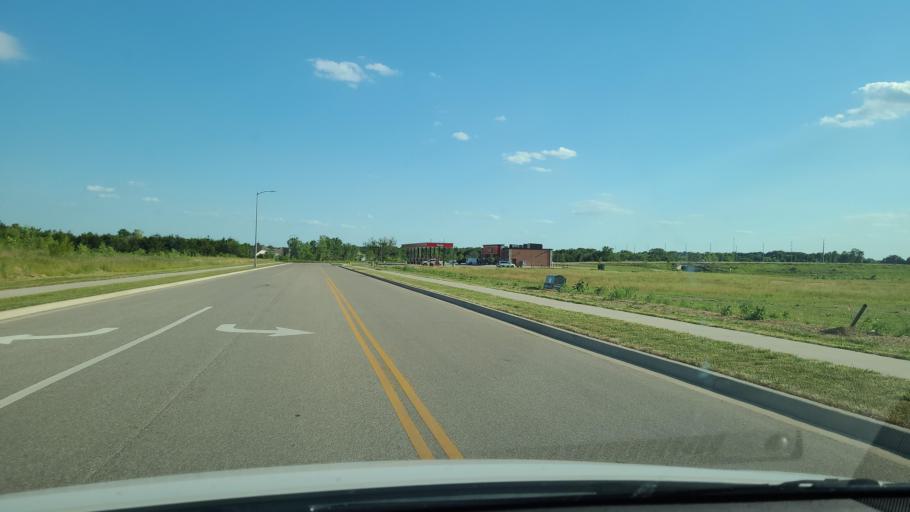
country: US
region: Kansas
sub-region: Douglas County
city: Lawrence
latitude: 38.9622
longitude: -95.3296
